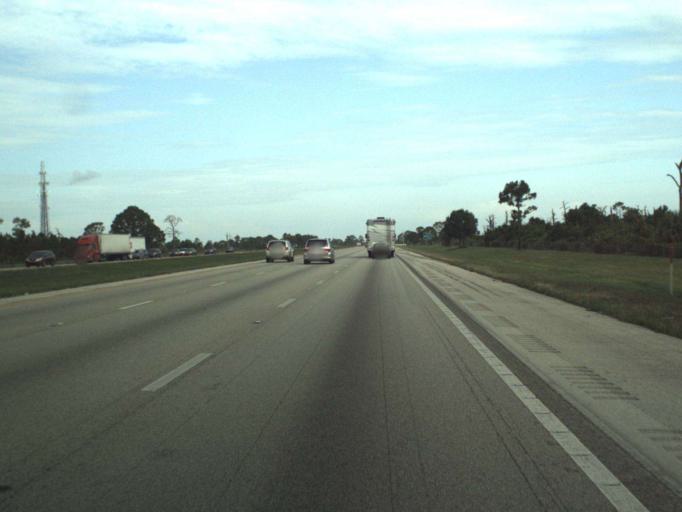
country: US
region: Florida
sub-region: Martin County
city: Palm City
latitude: 27.1444
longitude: -80.3742
